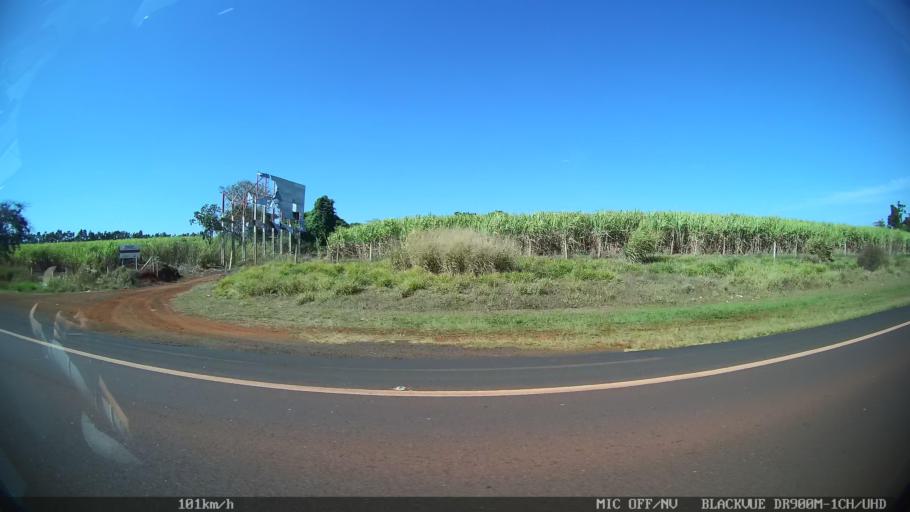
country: BR
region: Sao Paulo
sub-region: Franca
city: Franca
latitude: -20.6501
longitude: -47.4851
